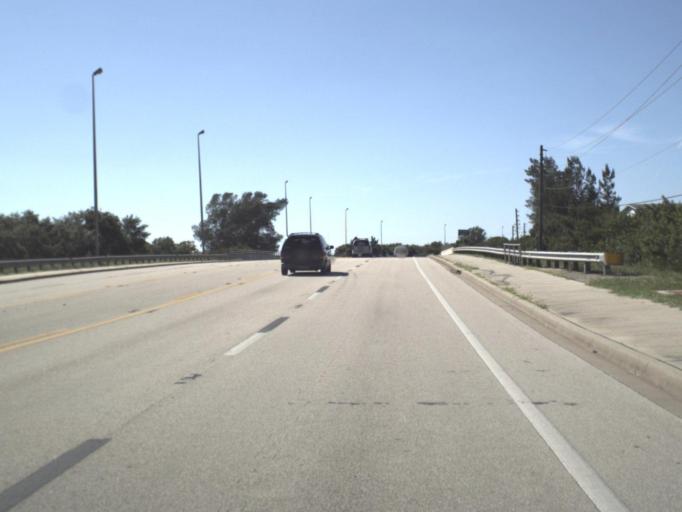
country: US
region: Florida
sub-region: Charlotte County
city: Manasota Key
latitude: 26.9387
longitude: -82.3438
